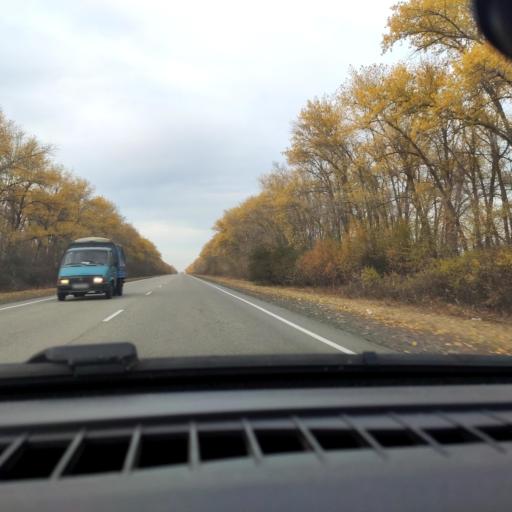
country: RU
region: Voronezj
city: Ostrogozhsk
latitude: 50.9882
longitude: 38.9971
